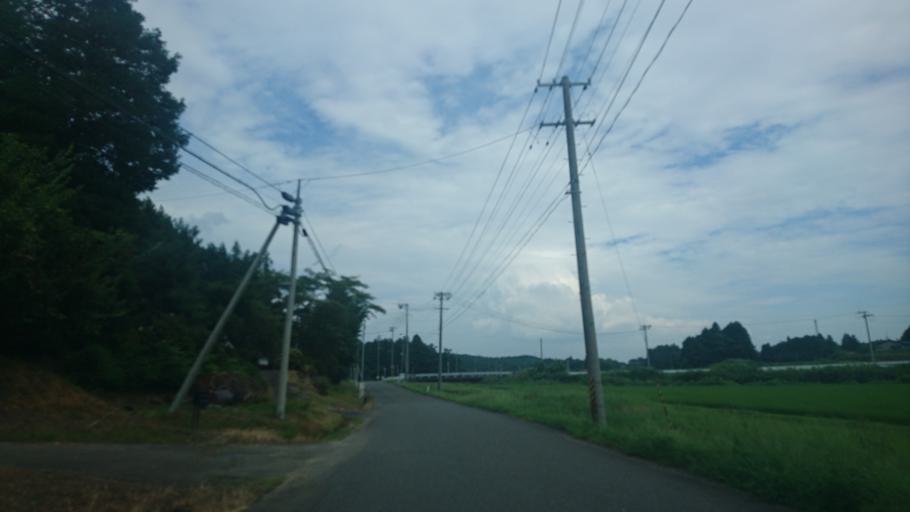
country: JP
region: Miyagi
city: Furukawa
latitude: 38.7684
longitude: 140.9517
